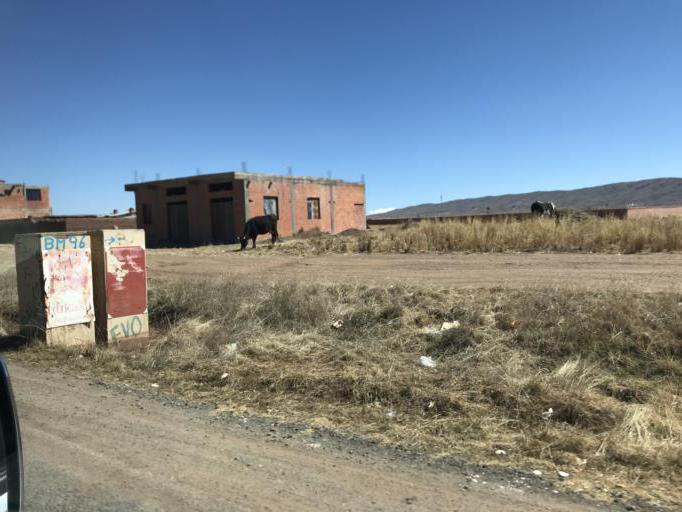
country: BO
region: La Paz
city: Tiahuanaco
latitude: -16.5710
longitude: -68.6727
